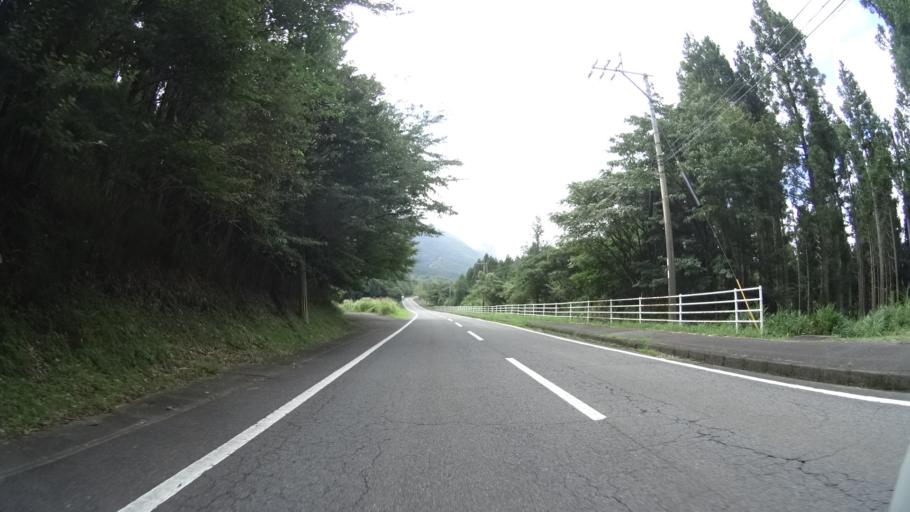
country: JP
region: Oita
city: Beppu
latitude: 33.3202
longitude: 131.4141
